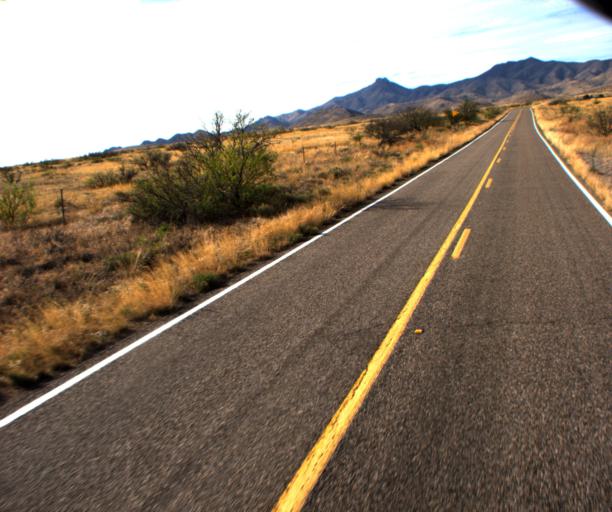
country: US
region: Arizona
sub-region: Cochise County
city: Willcox
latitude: 32.1199
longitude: -109.5550
